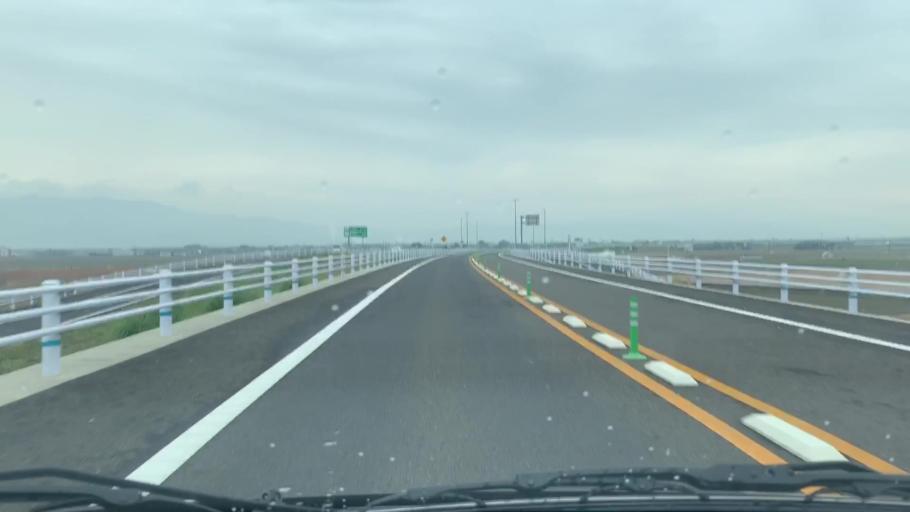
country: JP
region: Saga Prefecture
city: Saga-shi
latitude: 33.2214
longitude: 130.2151
